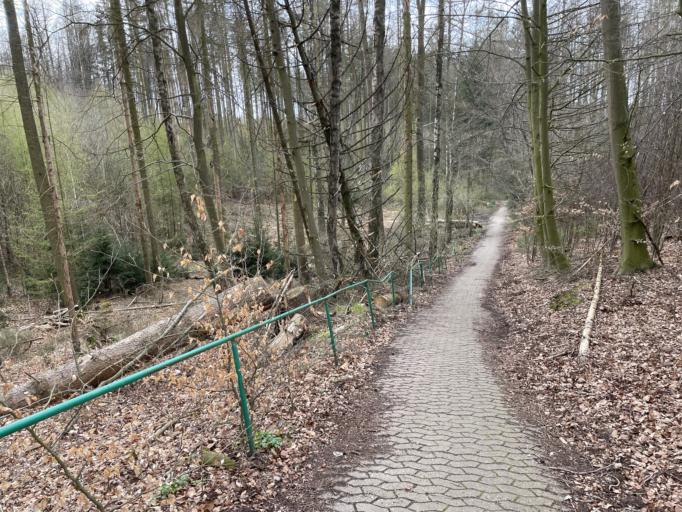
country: DE
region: North Rhine-Westphalia
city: Porta Westfalica
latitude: 52.2299
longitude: 8.9313
